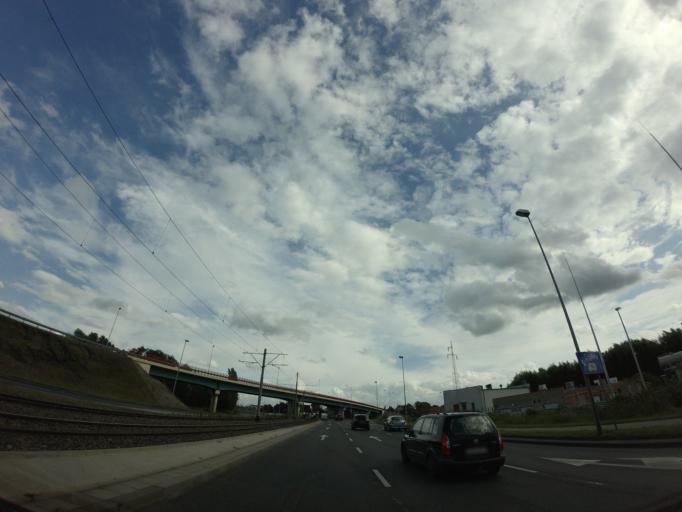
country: PL
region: West Pomeranian Voivodeship
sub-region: Szczecin
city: Szczecin
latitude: 53.3872
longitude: 14.6275
